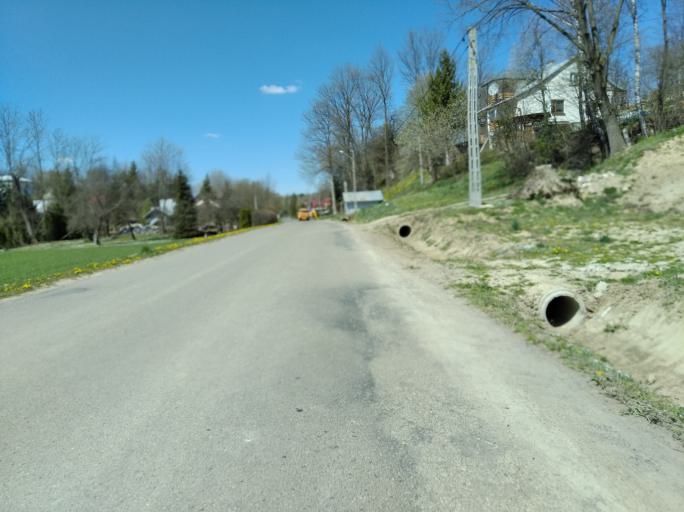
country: PL
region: Subcarpathian Voivodeship
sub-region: Powiat brzozowski
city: Jablonka
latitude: 49.7096
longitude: 22.1429
